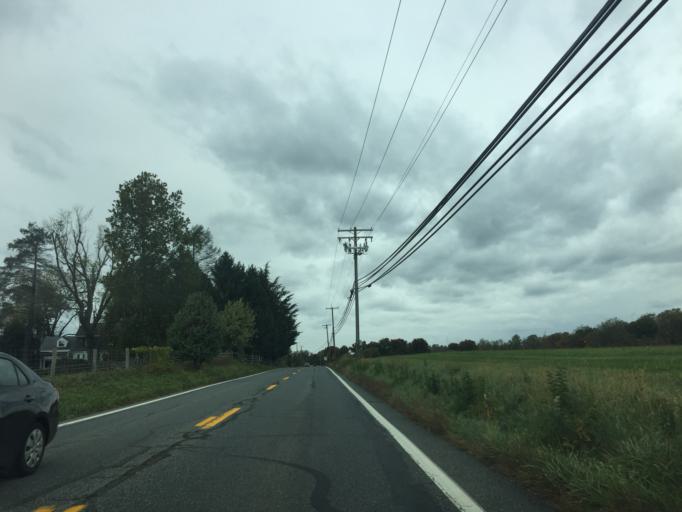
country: US
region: Maryland
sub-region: Harford County
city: Riverside
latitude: 39.5202
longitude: -76.2650
